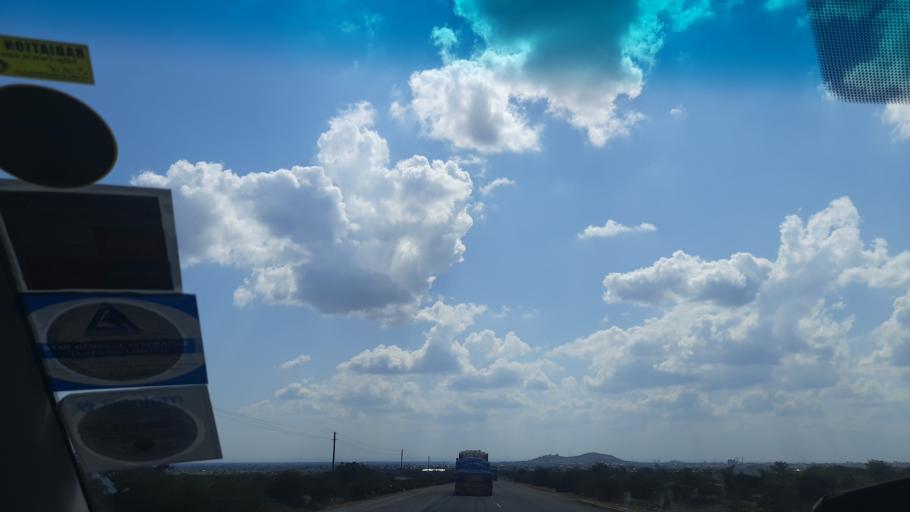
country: TZ
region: Singida
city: Kintinku
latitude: -5.9791
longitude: 35.3455
